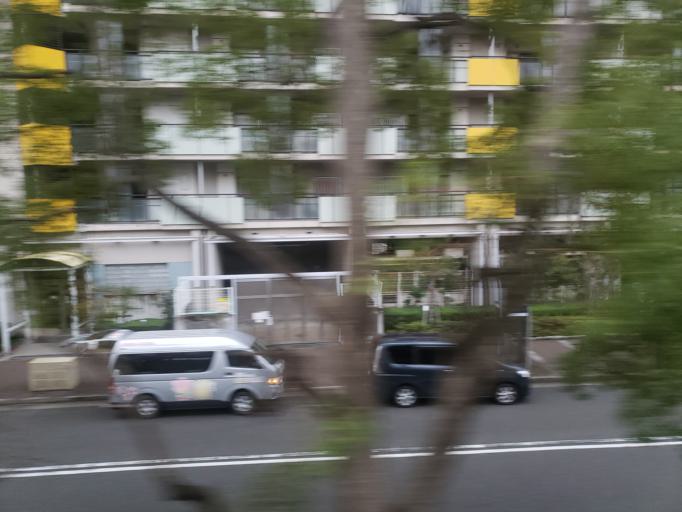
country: JP
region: Hyogo
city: Kobe
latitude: 34.6559
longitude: 135.1424
